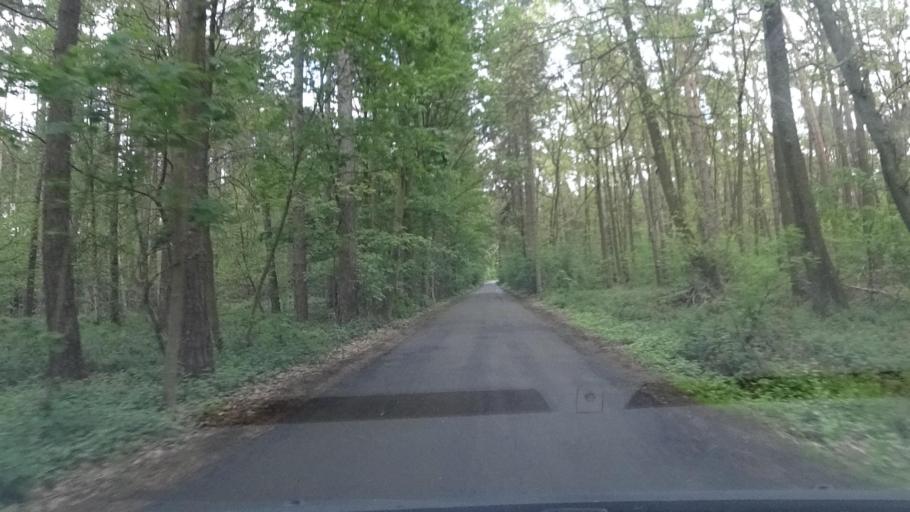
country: BE
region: Wallonia
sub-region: Province du Brabant Wallon
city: Court-Saint-Etienne
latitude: 50.6477
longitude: 4.5824
